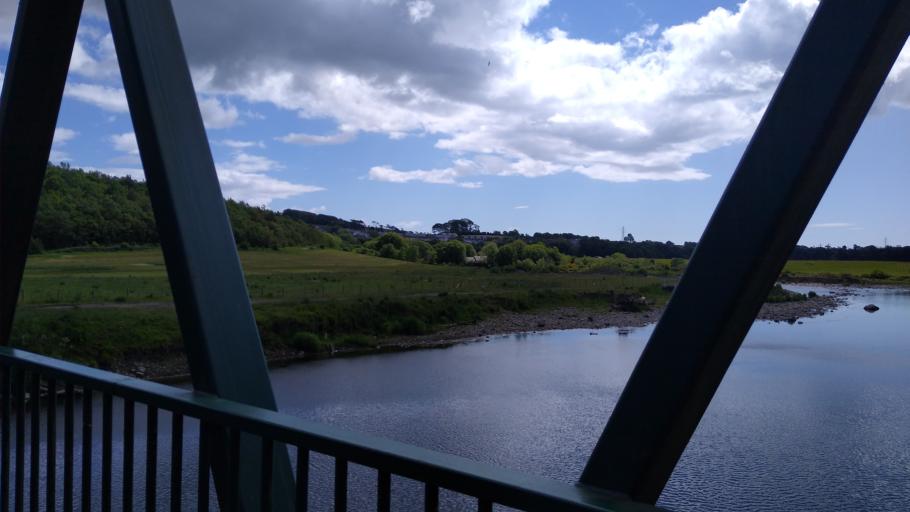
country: GB
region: England
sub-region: Cumbria
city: Flimby
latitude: 54.6604
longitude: -3.4942
